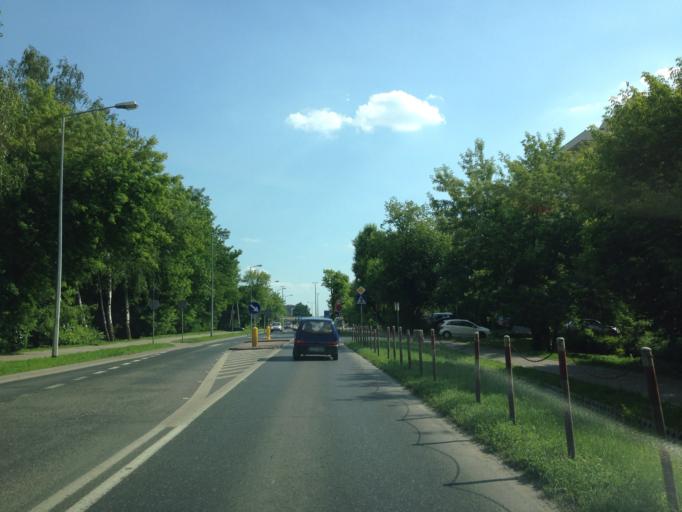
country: PL
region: Masovian Voivodeship
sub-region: Warszawa
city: Bemowo
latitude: 52.2477
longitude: 20.8979
